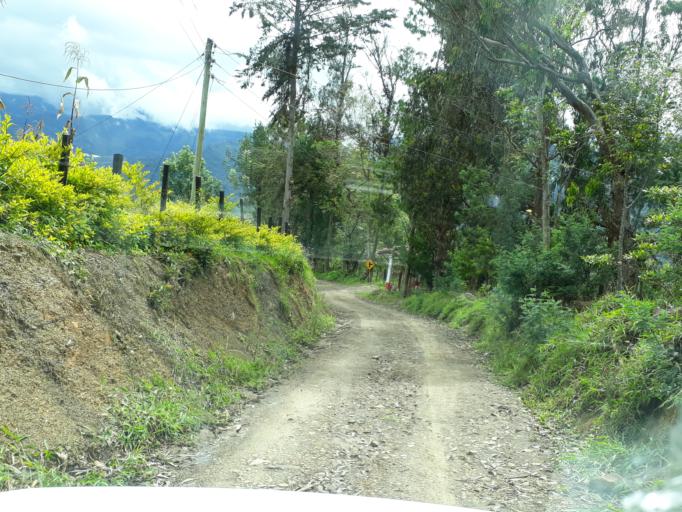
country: CO
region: Cundinamarca
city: Junin
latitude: 4.7990
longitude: -73.6506
